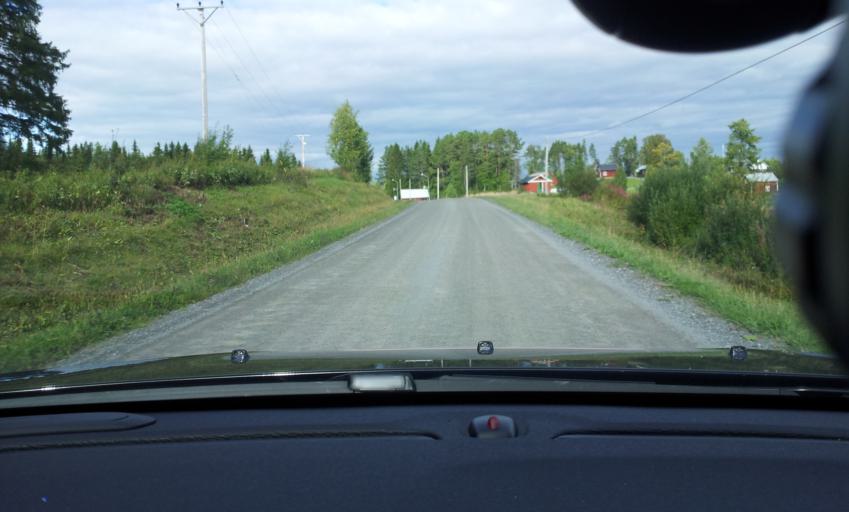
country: SE
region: Jaemtland
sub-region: Krokoms Kommun
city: Valla
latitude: 63.2543
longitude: 13.9481
